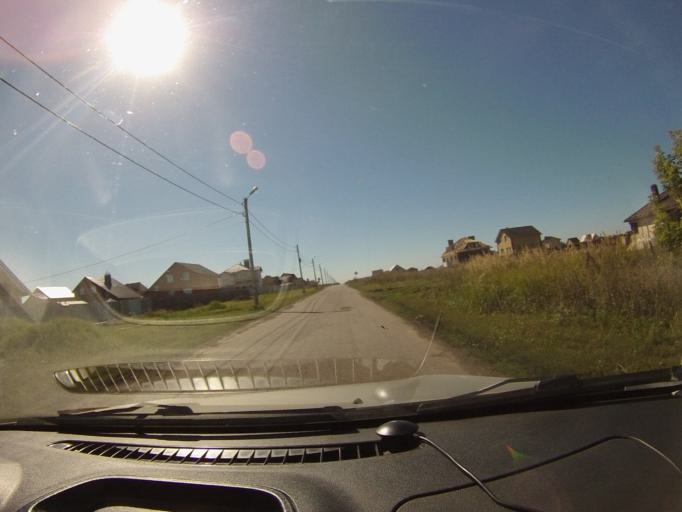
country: RU
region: Tambov
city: Komsomolets
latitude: 52.7749
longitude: 41.3639
